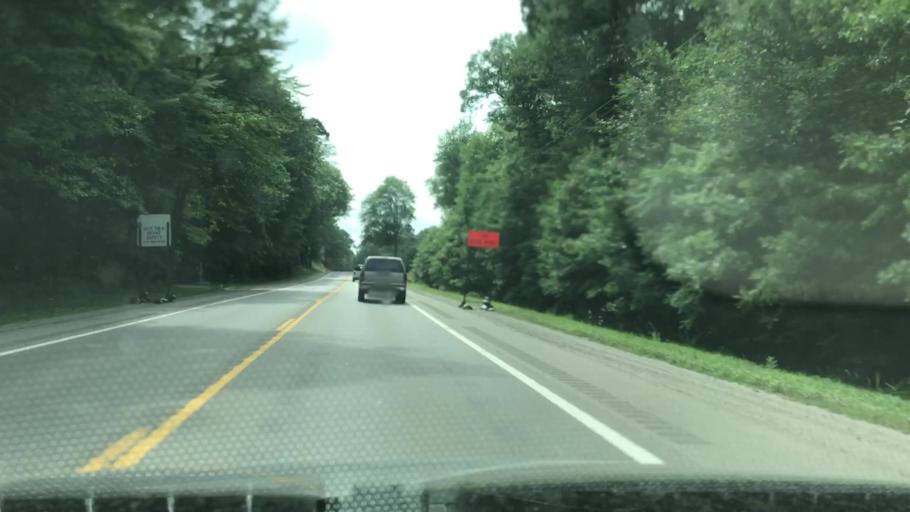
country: US
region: Michigan
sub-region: Muskegon County
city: Fruitport
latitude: 43.0739
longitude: -86.1317
